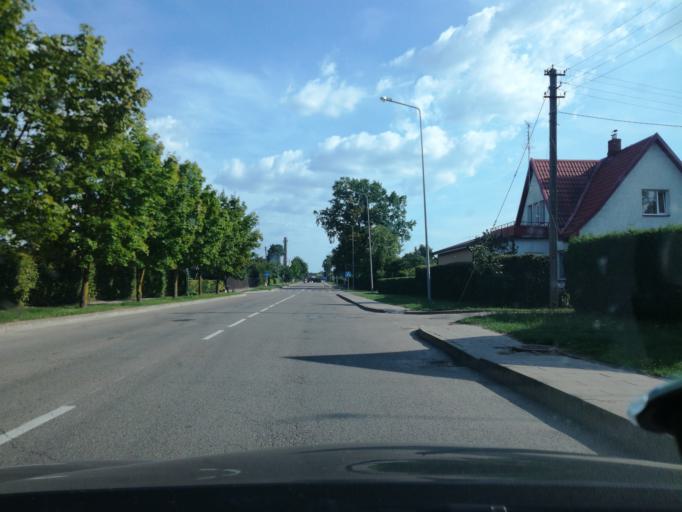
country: LT
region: Marijampoles apskritis
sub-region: Marijampole Municipality
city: Marijampole
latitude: 54.5428
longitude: 23.3490
